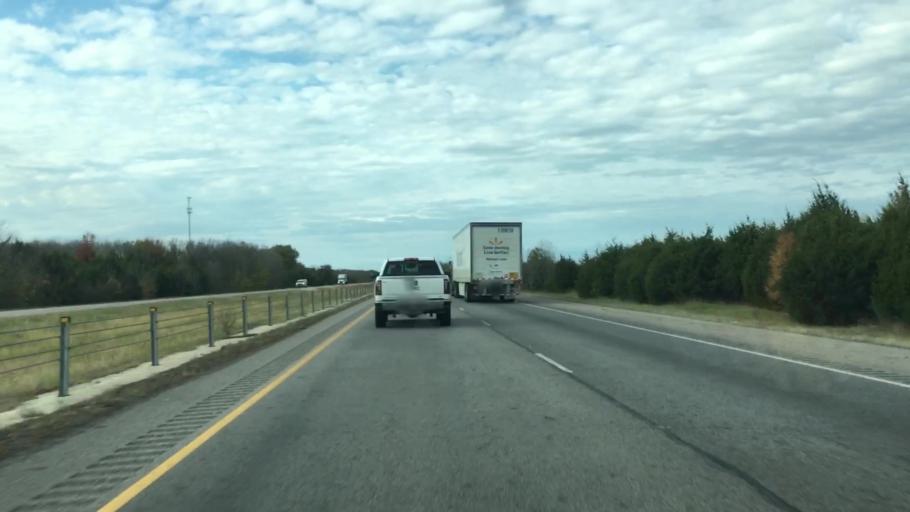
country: US
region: Arkansas
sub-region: Conway County
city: Morrilton
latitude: 35.2011
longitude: -92.8065
